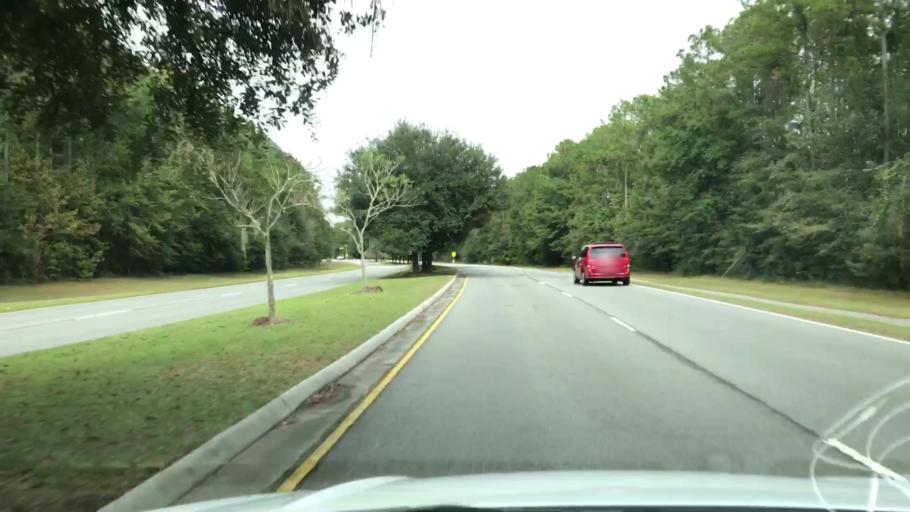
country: US
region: South Carolina
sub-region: Beaufort County
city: Bluffton
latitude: 32.2412
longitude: -80.9024
